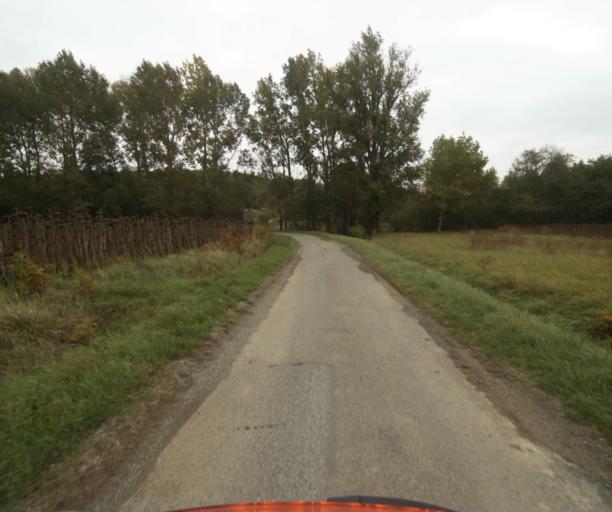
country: FR
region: Midi-Pyrenees
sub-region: Departement de la Haute-Garonne
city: Grenade
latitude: 43.7782
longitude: 1.2318
